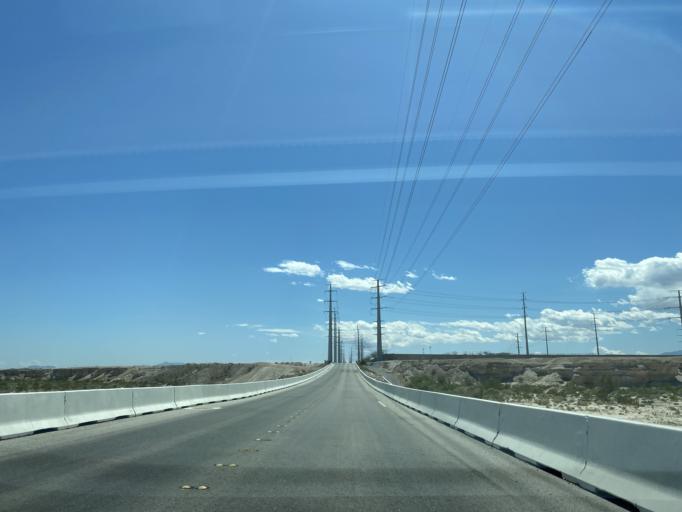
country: US
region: Nevada
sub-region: Clark County
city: North Las Vegas
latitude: 36.3266
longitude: -115.2071
